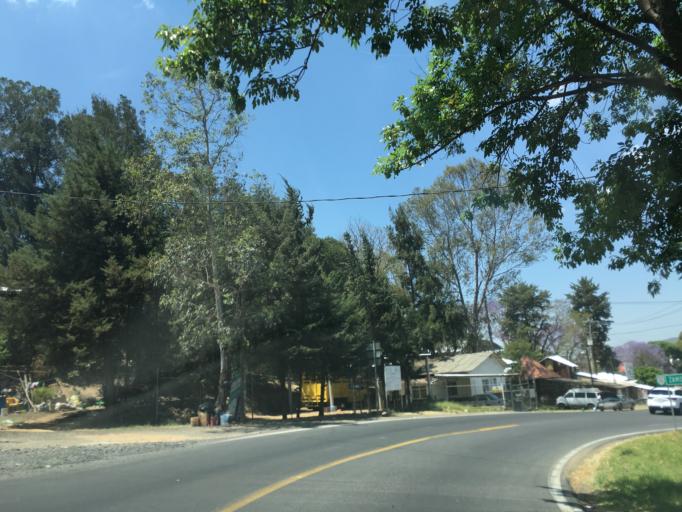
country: MX
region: Michoacan
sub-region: Chilchota
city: Tacuro (Santa Maria Tacuro)
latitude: 19.8512
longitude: -102.0319
